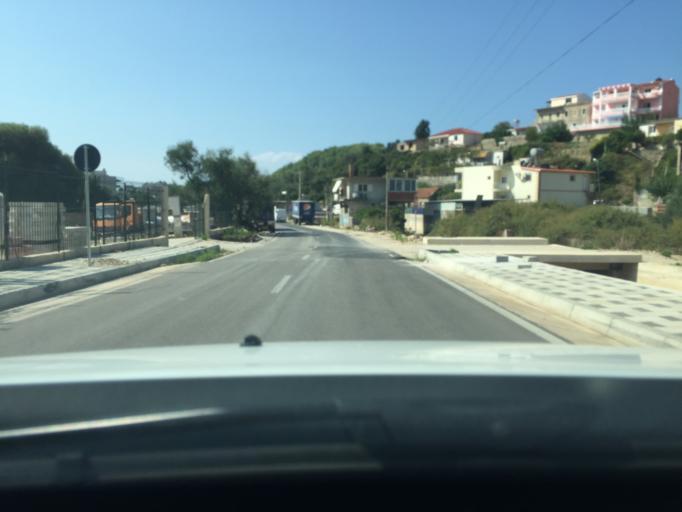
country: AL
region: Vlore
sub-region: Rrethi i Vlores
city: Himare
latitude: 40.1085
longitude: 19.7424
